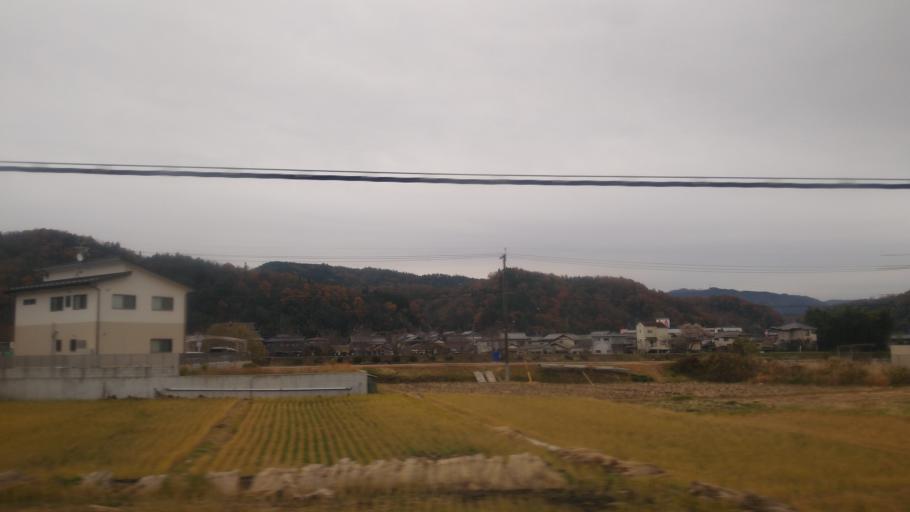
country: JP
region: Gifu
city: Mizunami
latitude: 35.3704
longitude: 137.2593
